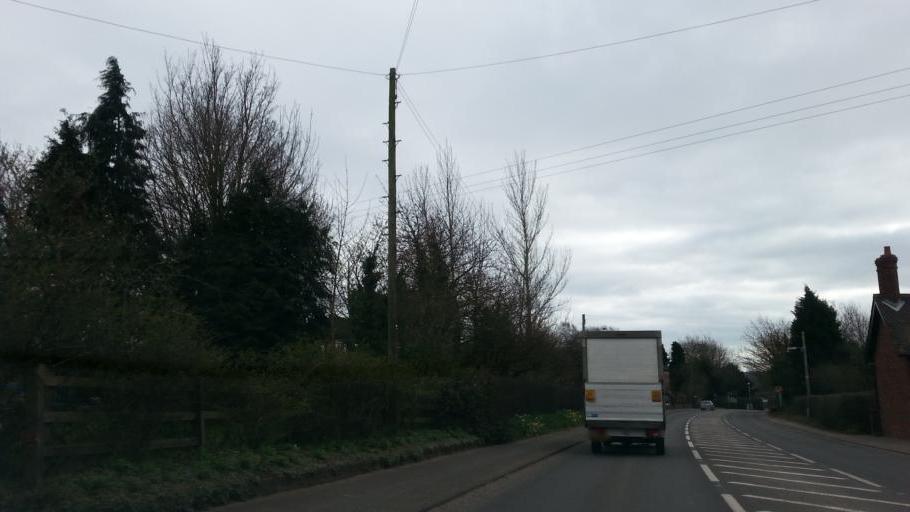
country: GB
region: England
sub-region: Staffordshire
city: Stafford
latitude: 52.8643
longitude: -2.0792
